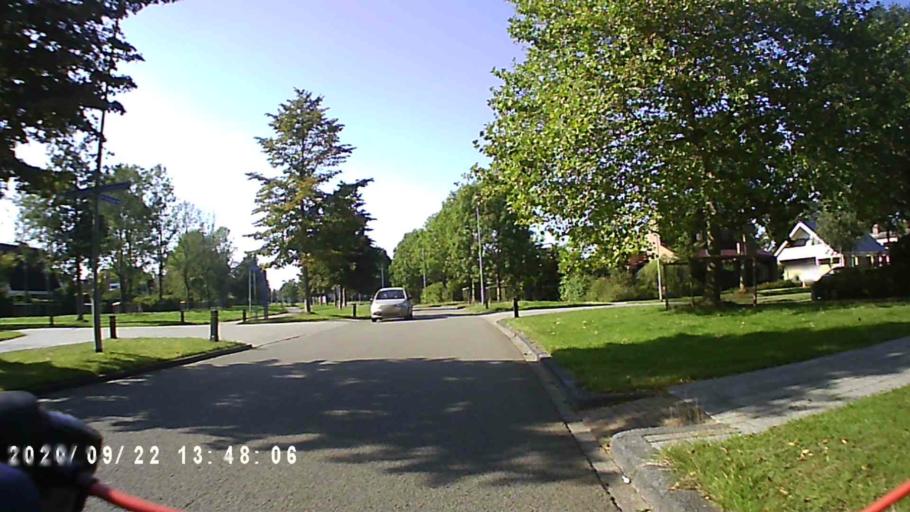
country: NL
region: Groningen
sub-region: Gemeente Leek
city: Leek
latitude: 53.1407
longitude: 6.4070
